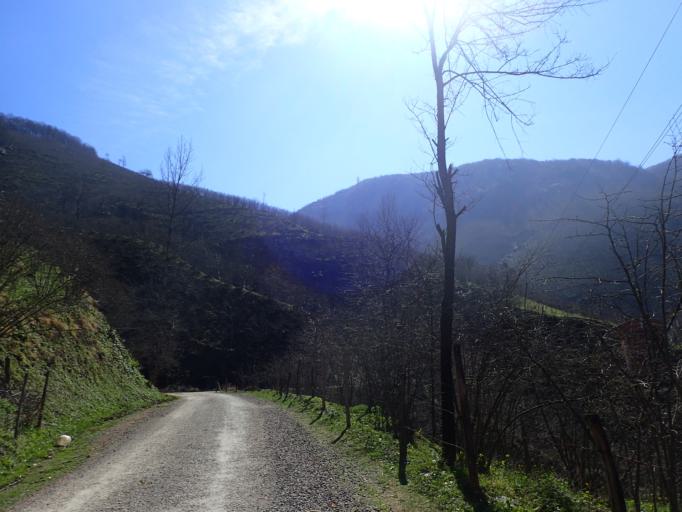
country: TR
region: Ordu
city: Catalpinar
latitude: 40.8641
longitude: 37.4944
